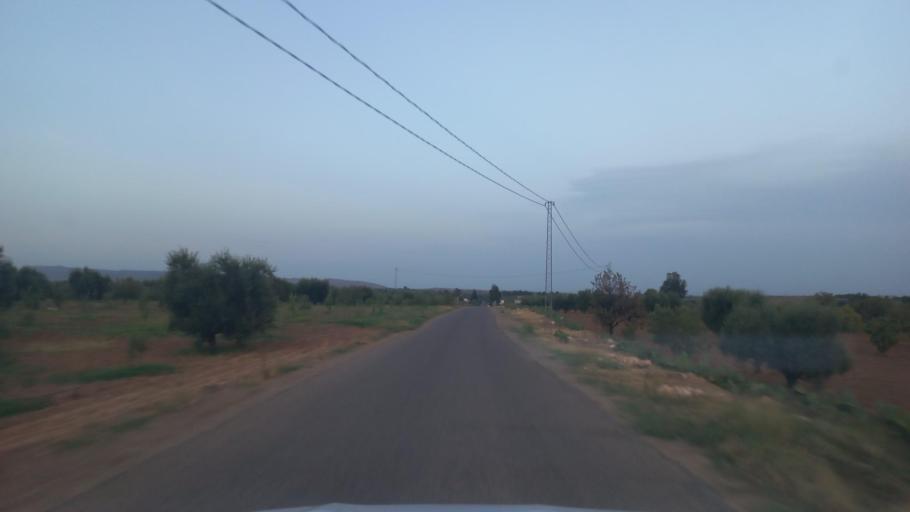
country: TN
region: Al Qasrayn
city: Kasserine
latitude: 35.2198
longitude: 9.0487
